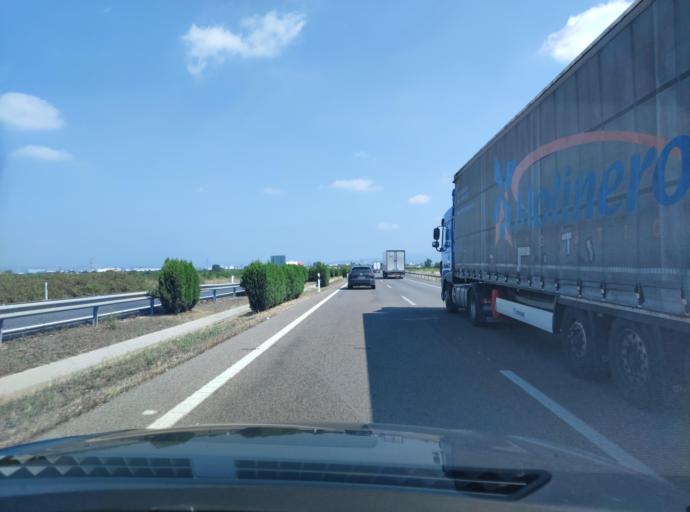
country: ES
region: Valencia
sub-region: Provincia de Castello
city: Alquerias del Nino Perdido
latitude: 39.9122
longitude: -0.1346
